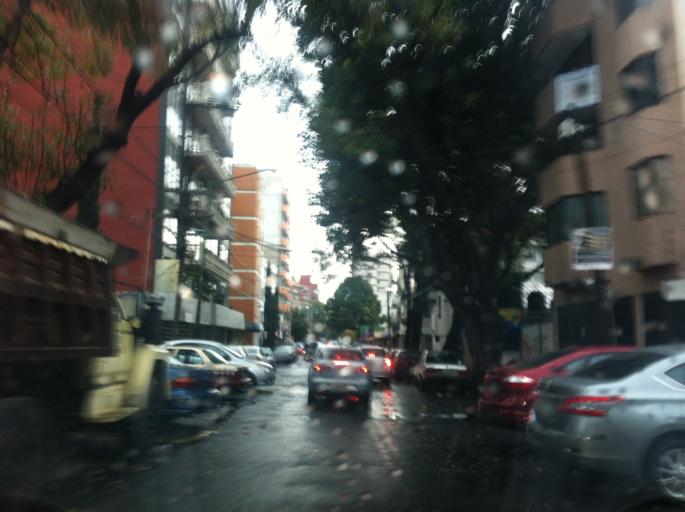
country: MX
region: Mexico City
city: Colonia del Valle
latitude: 19.3668
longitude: -99.1780
